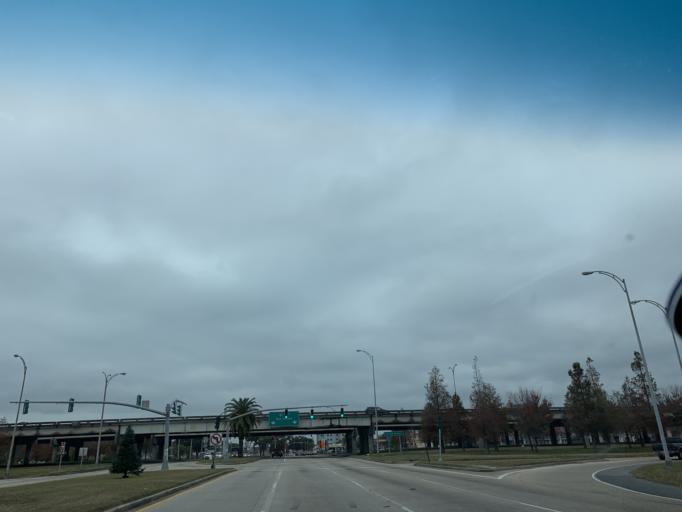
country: US
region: Louisiana
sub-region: Saint Bernard Parish
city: Arabi
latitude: 30.0454
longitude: -89.9604
